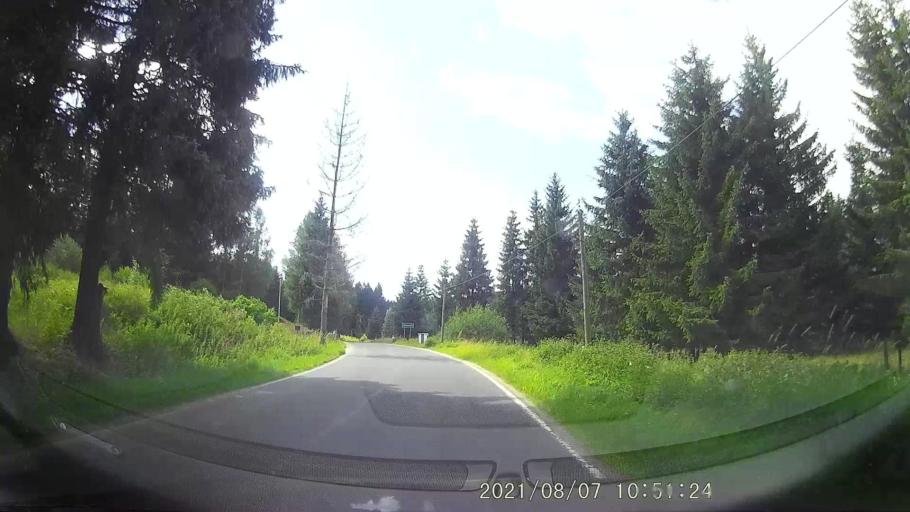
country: PL
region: Lower Silesian Voivodeship
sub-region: Powiat klodzki
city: Polanica-Zdroj
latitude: 50.2895
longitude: 16.4684
